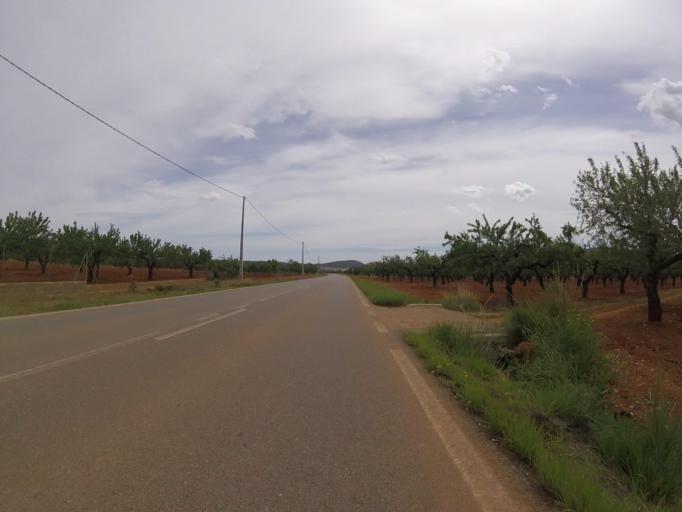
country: ES
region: Valencia
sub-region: Provincia de Castello
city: Cabanes
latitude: 40.1672
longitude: 0.0054
